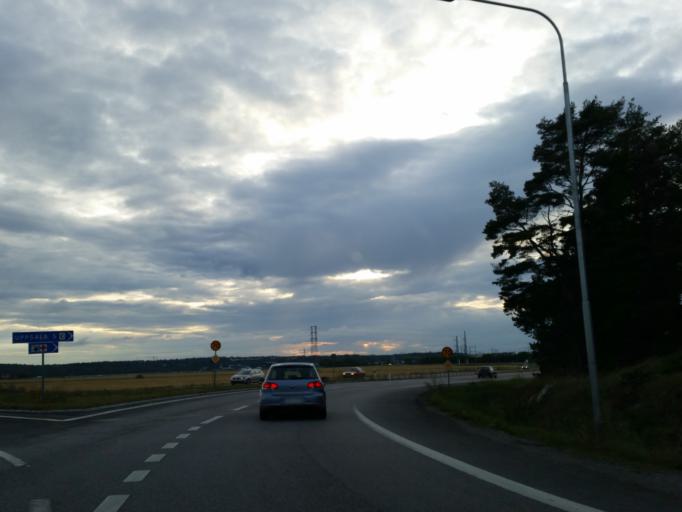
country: SE
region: Uppsala
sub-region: Uppsala Kommun
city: Saevja
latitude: 59.8432
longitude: 17.7104
